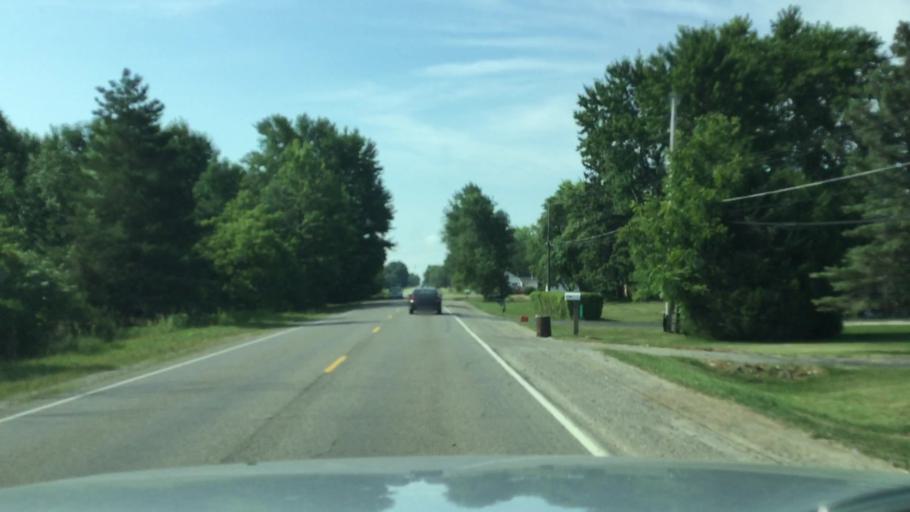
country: US
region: Michigan
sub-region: Genesee County
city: Flushing
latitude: 43.1131
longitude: -83.8138
